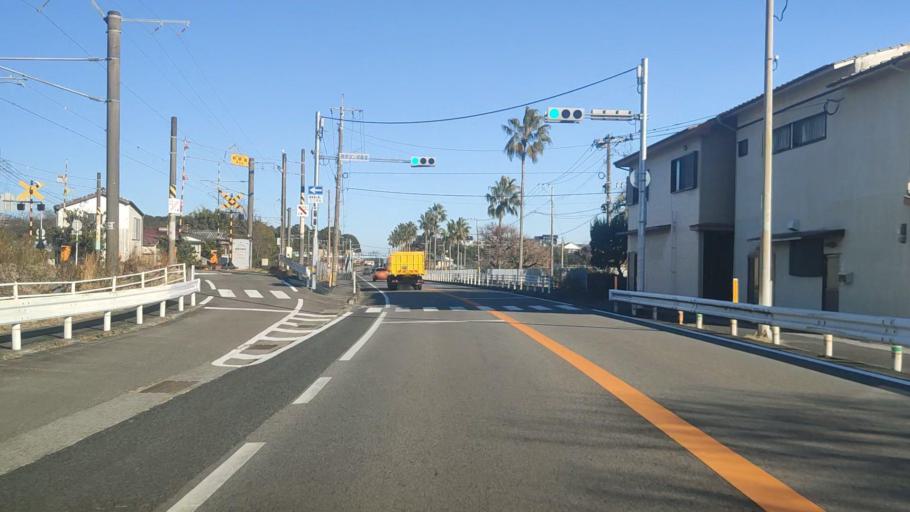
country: JP
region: Miyazaki
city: Nobeoka
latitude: 32.5140
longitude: 131.6824
